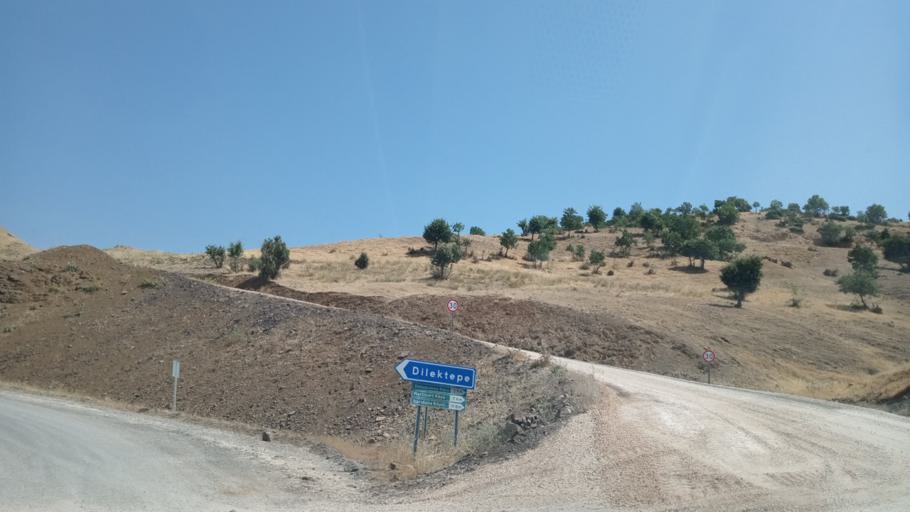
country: TR
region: Siirt
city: Dilektepe
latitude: 38.0715
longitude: 41.8304
